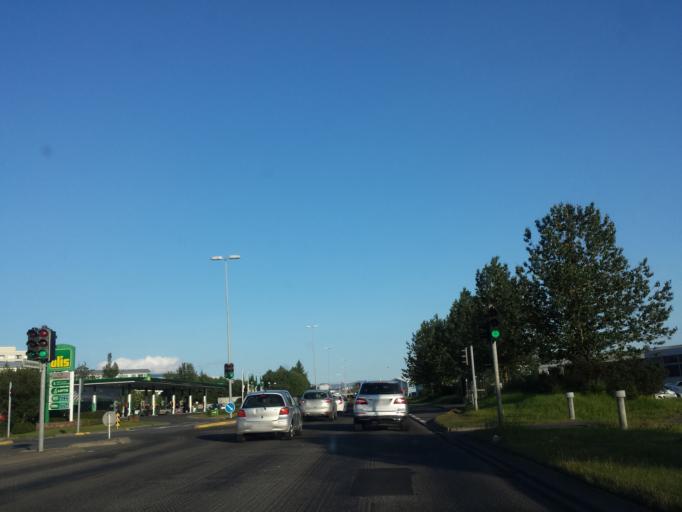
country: IS
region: Capital Region
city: Reykjavik
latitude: 64.1331
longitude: -21.8690
